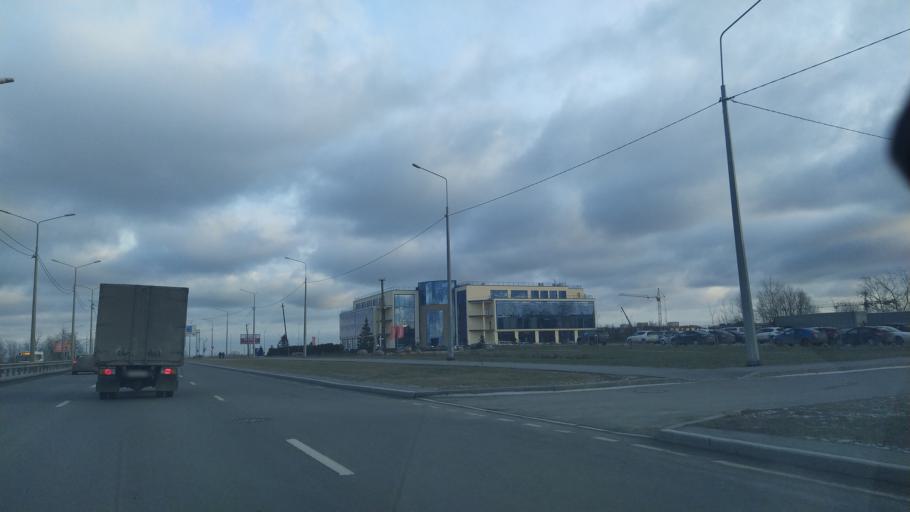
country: RU
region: St.-Petersburg
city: Aleksandrovskaya
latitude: 59.7612
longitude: 30.3668
